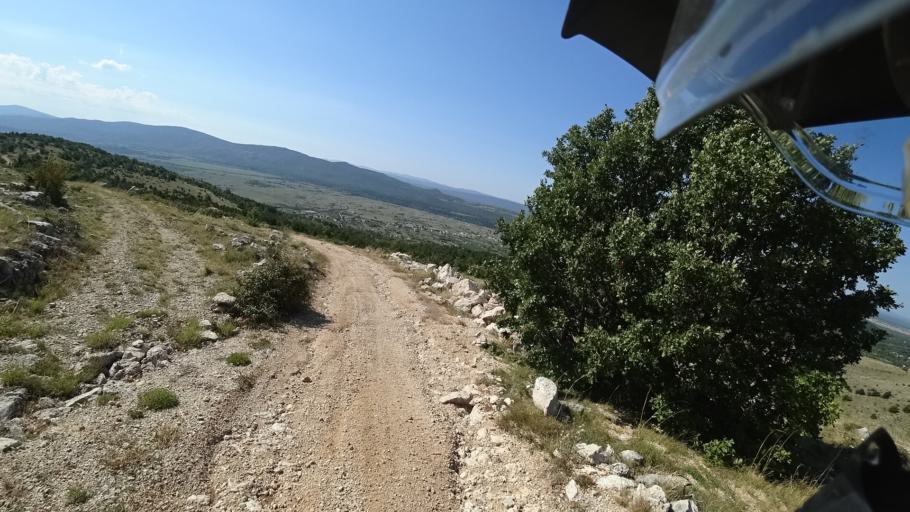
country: HR
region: Sibensko-Kniniska
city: Drnis
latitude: 43.8799
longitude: 16.1800
